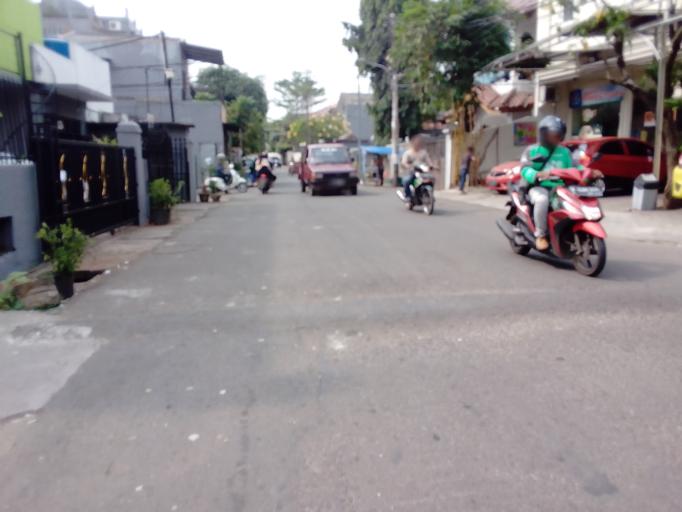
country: ID
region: Jakarta Raya
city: Jakarta
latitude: -6.2004
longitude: 106.8106
